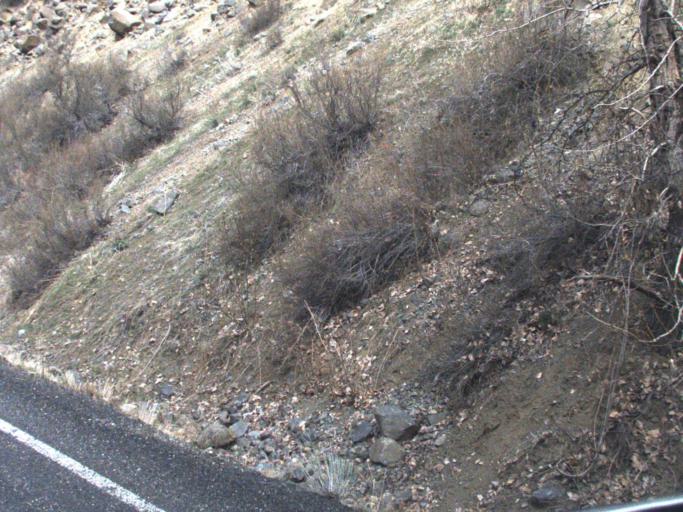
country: US
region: Washington
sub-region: Yakima County
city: Tieton
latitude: 46.7676
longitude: -120.8355
